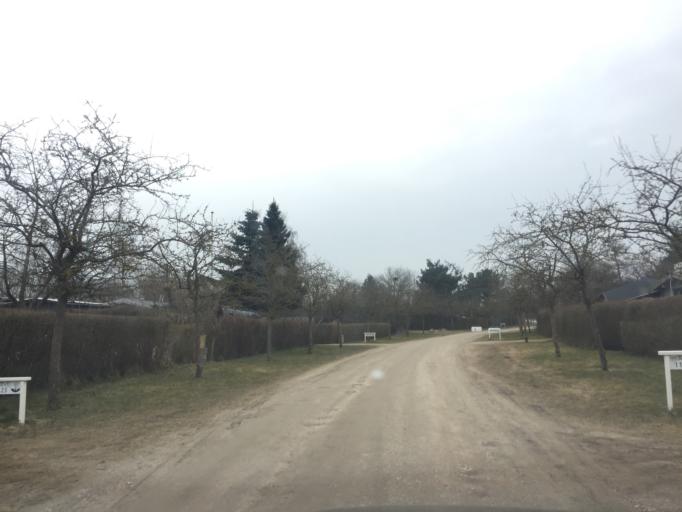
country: DK
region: Capital Region
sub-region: Hoje-Taastrup Kommune
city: Flong
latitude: 55.6415
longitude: 12.1901
